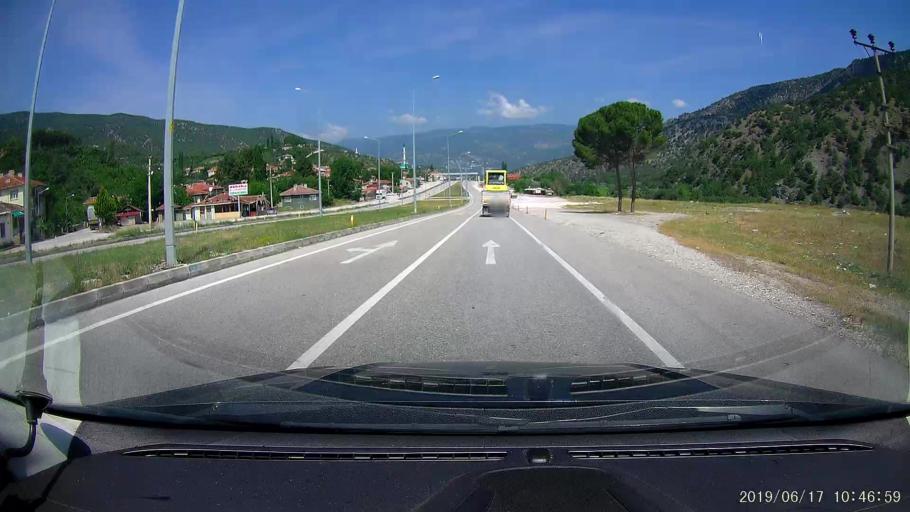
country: TR
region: Corum
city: Hacihamza
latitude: 41.0736
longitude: 34.4544
